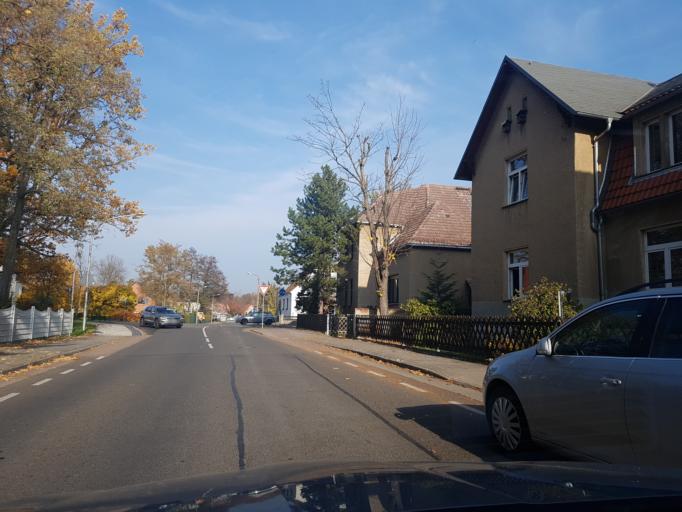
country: DE
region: Brandenburg
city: Elsterwerda
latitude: 51.4633
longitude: 13.5215
